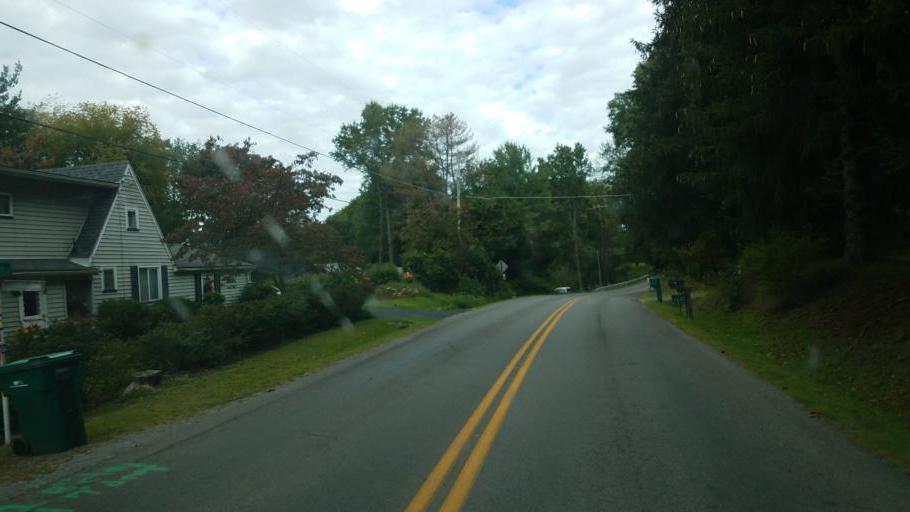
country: US
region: Pennsylvania
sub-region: Crawford County
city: Pymatuning Central
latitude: 41.5227
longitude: -80.4687
